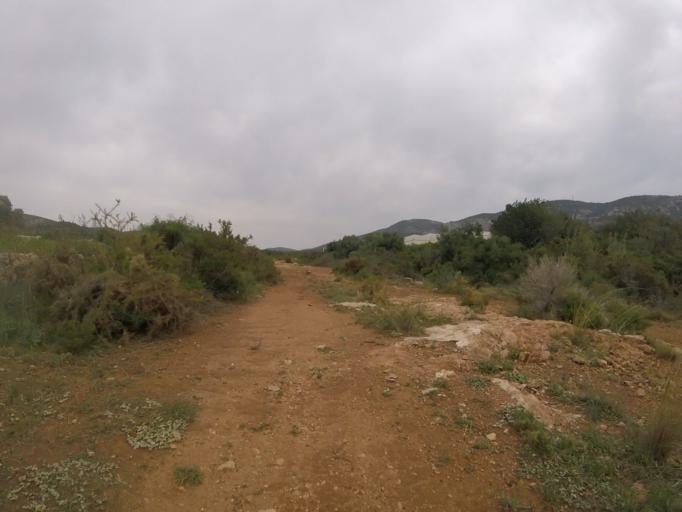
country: ES
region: Valencia
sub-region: Provincia de Castello
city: Alcala de Xivert
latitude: 40.2777
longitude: 0.2562
